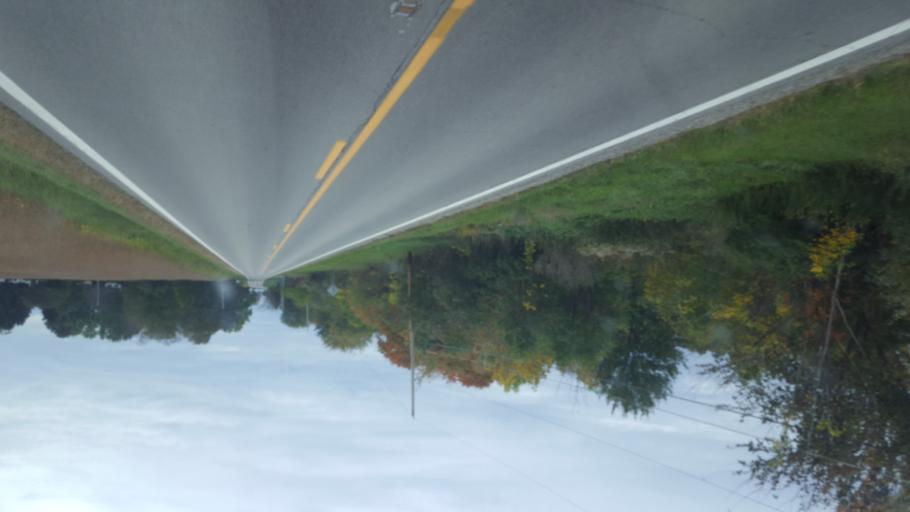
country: US
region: Ohio
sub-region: Huron County
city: Wakeman
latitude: 41.3075
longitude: -82.3677
